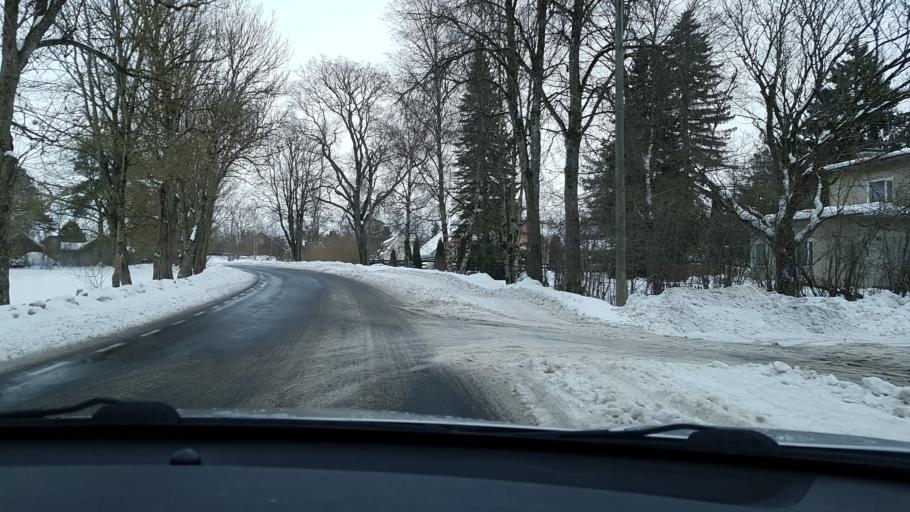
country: EE
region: Jaervamaa
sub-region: Jaerva-Jaani vald
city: Jarva-Jaani
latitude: 59.1426
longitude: 25.7518
